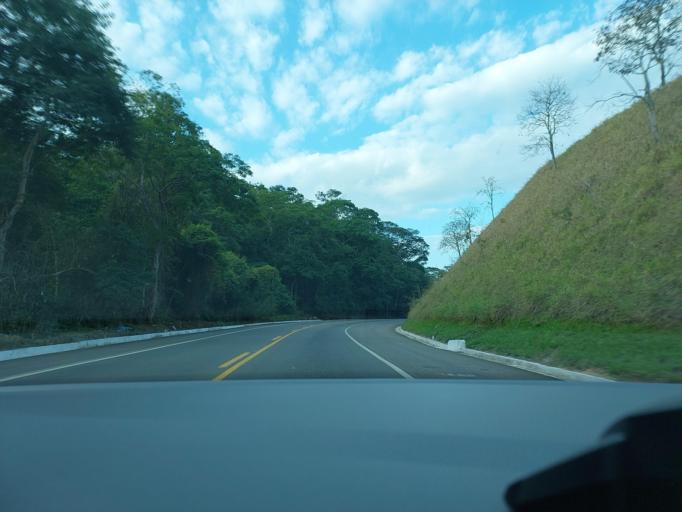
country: BR
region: Minas Gerais
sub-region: Muriae
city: Muriae
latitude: -21.1289
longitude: -42.2903
